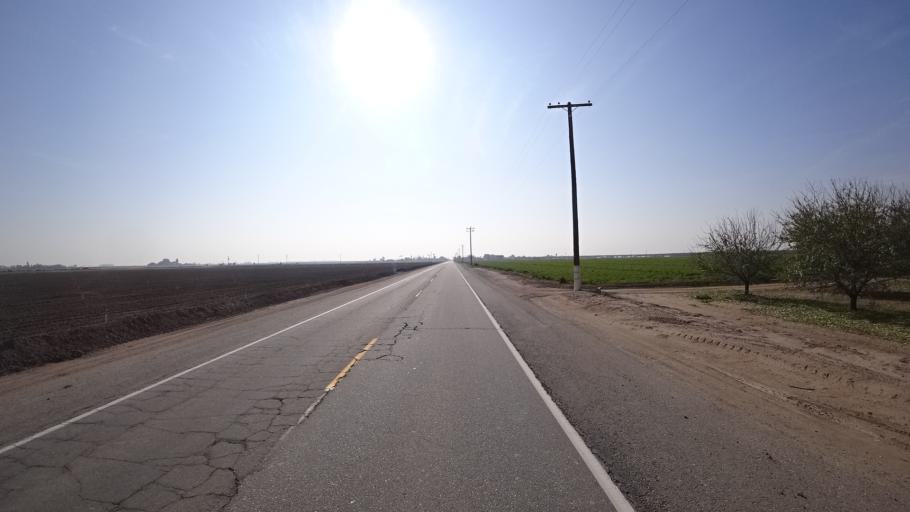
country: US
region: California
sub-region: Kern County
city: Greenacres
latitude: 35.2772
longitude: -119.1098
